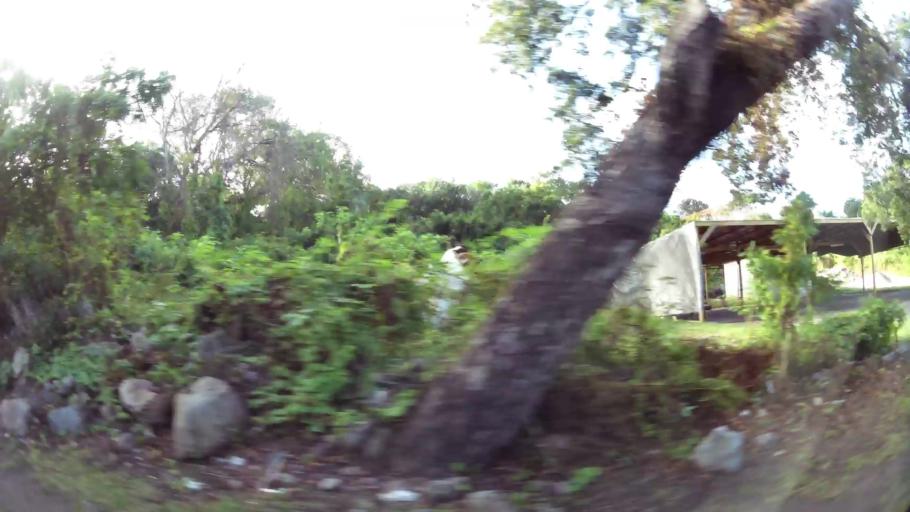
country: KN
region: Saint Paul Charlestown
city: Charlestown
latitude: 17.1329
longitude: -62.6243
